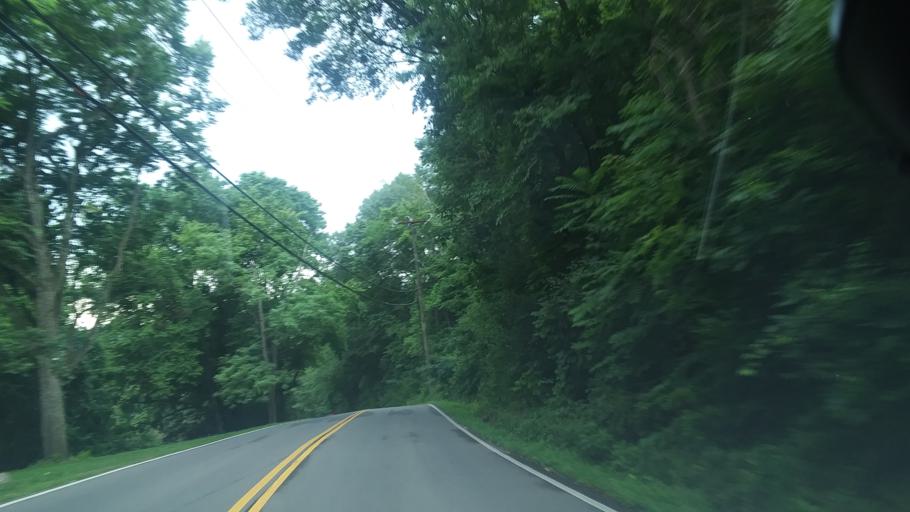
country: US
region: Tennessee
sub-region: Davidson County
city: Belle Meade
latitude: 36.0847
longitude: -86.9340
